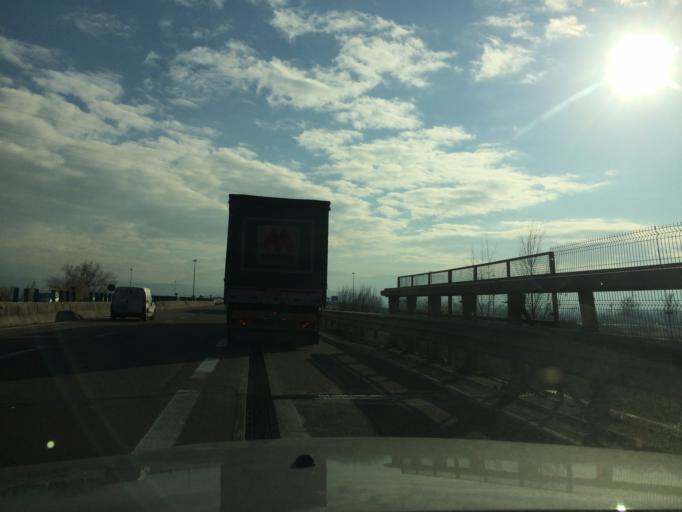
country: IT
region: Umbria
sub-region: Provincia di Terni
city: San Gemini
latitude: 42.5732
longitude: 12.5748
